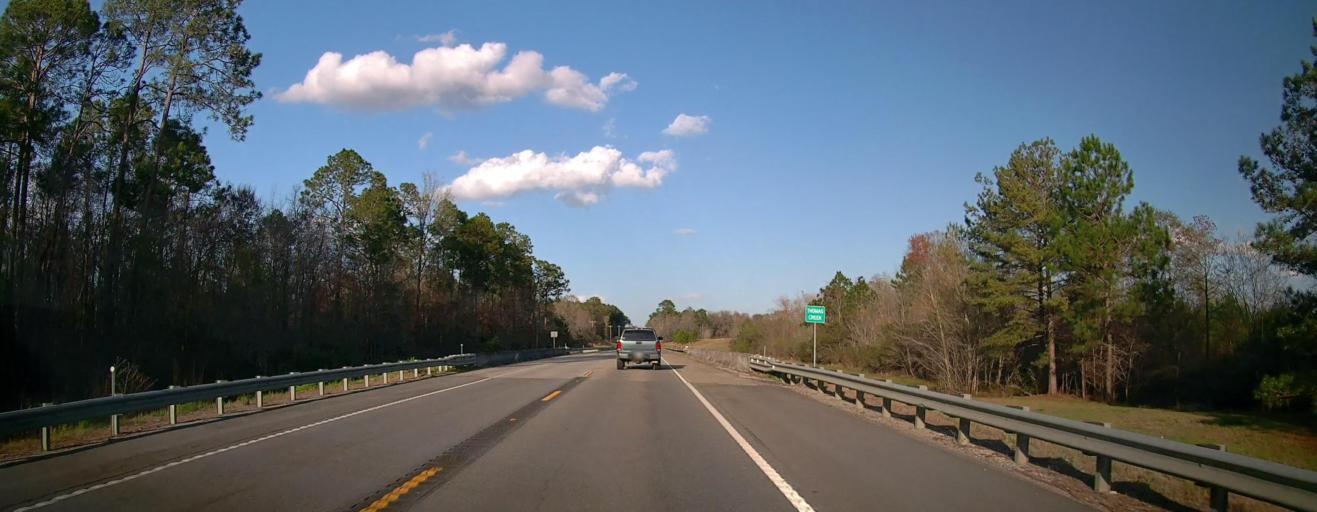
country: US
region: Georgia
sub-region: Tattnall County
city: Reidsville
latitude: 32.1300
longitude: -82.0514
